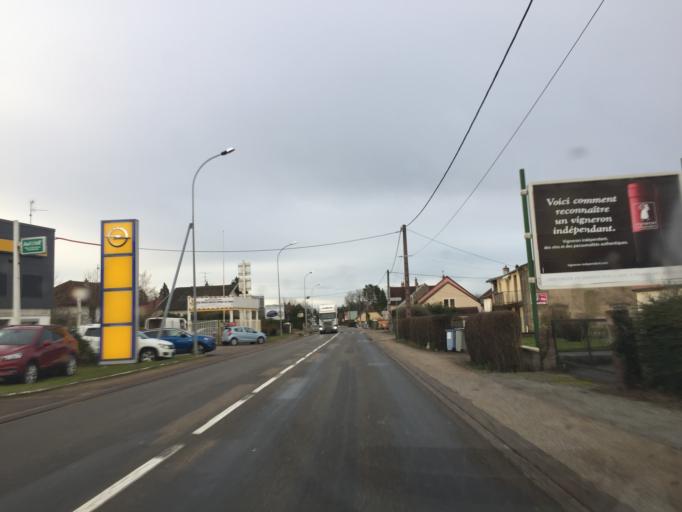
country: FR
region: Franche-Comte
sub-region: Departement du Jura
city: Dole
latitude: 47.0667
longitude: 5.4952
